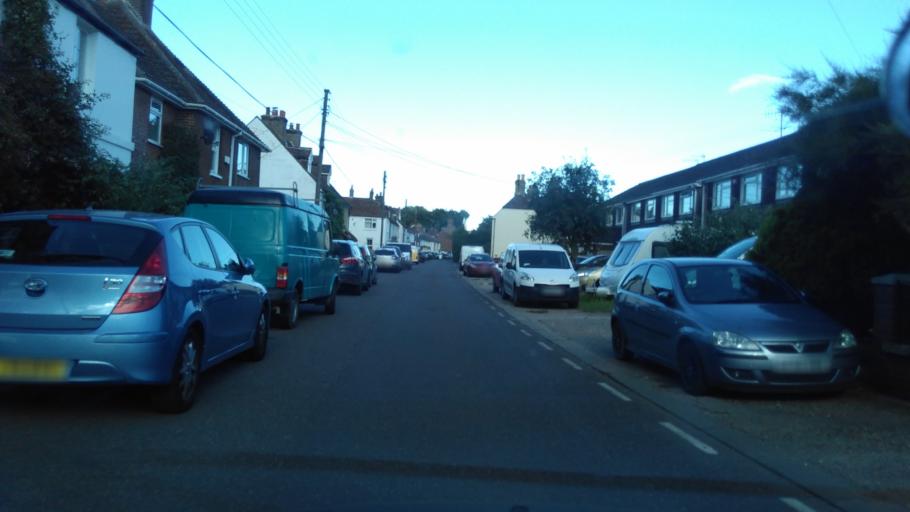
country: GB
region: England
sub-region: Kent
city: Chartham
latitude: 51.2540
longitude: 0.9978
